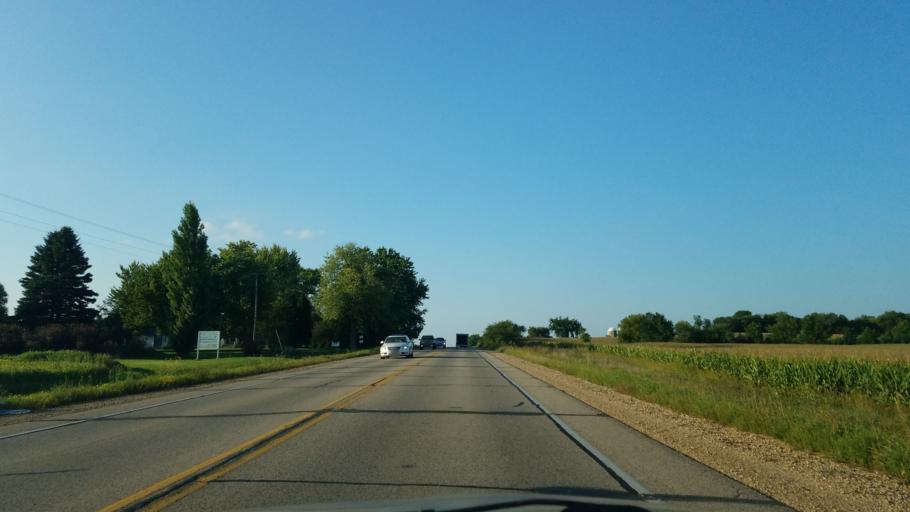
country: US
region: Wisconsin
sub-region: Saint Croix County
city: New Richmond
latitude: 45.0598
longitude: -92.5373
